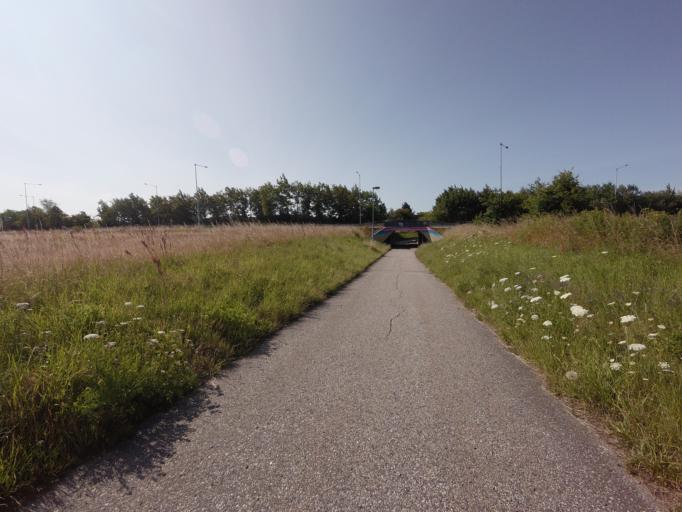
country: SE
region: Skane
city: Bjarred
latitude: 55.7263
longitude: 13.0297
